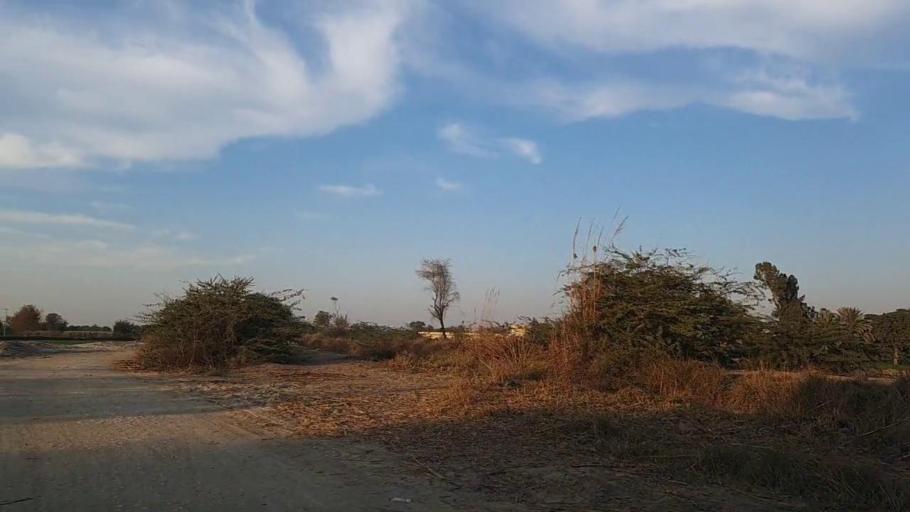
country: PK
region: Sindh
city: Bandhi
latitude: 26.5980
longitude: 68.3590
